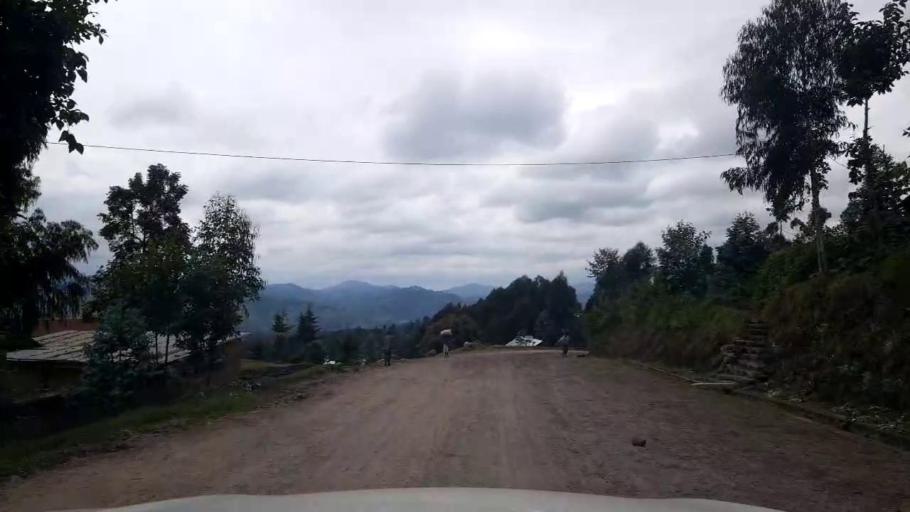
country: RW
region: Northern Province
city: Musanze
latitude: -1.5333
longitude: 29.5334
